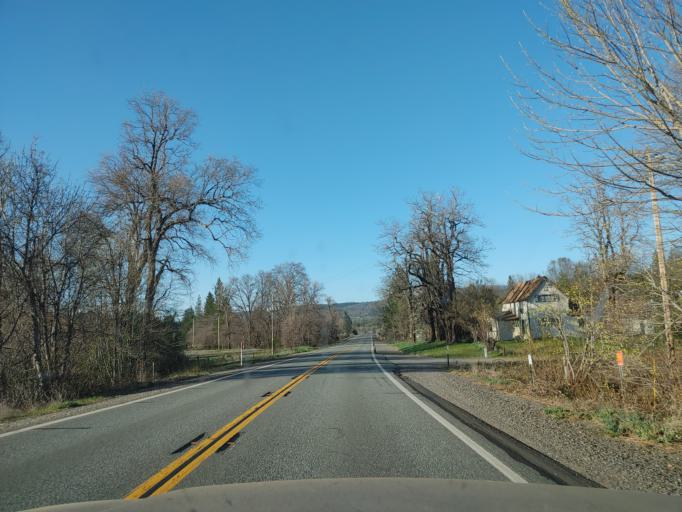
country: US
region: California
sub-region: Shasta County
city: Burney
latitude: 40.8147
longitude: -121.9382
